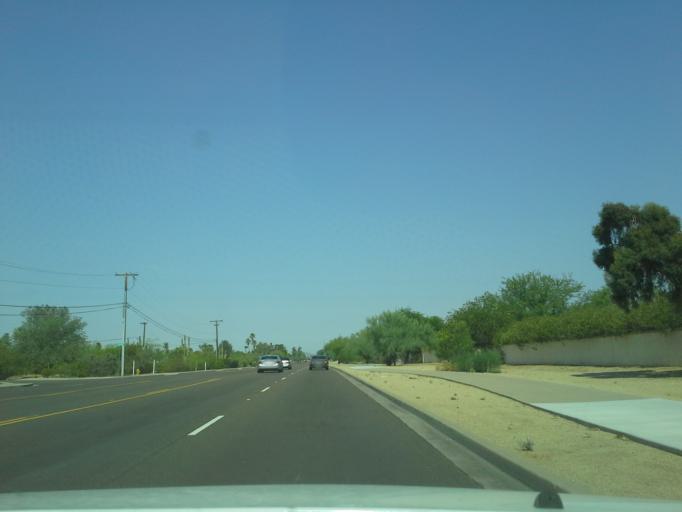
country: US
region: Arizona
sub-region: Maricopa County
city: Paradise Valley
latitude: 33.5967
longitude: -111.9115
